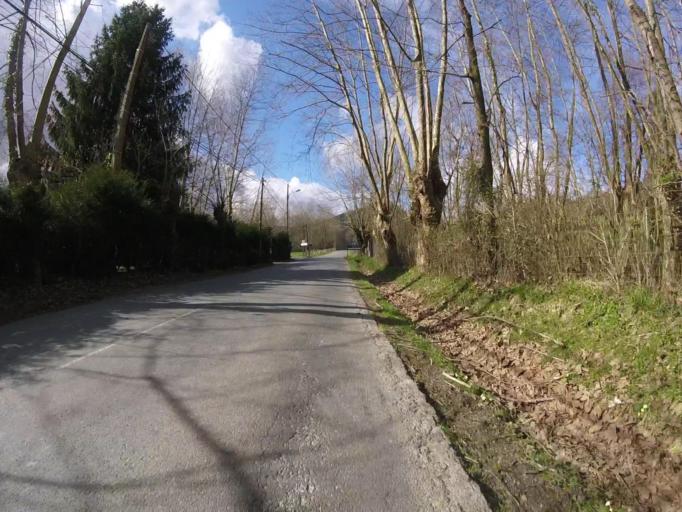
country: FR
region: Aquitaine
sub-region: Departement des Pyrenees-Atlantiques
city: Sare
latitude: 43.2855
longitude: -1.5839
